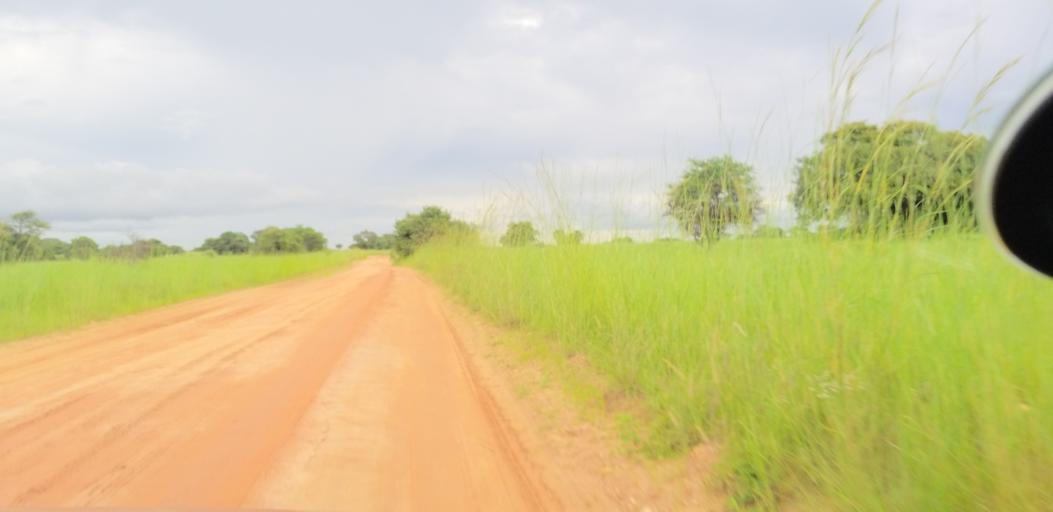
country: ZM
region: Lusaka
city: Chongwe
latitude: -15.1633
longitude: 28.4707
